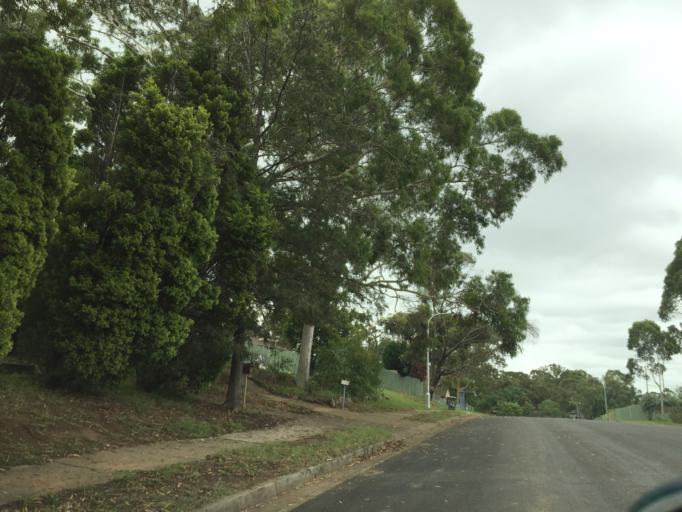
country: AU
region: New South Wales
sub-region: Blacktown
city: Blacktown
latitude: -33.7984
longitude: 150.9021
